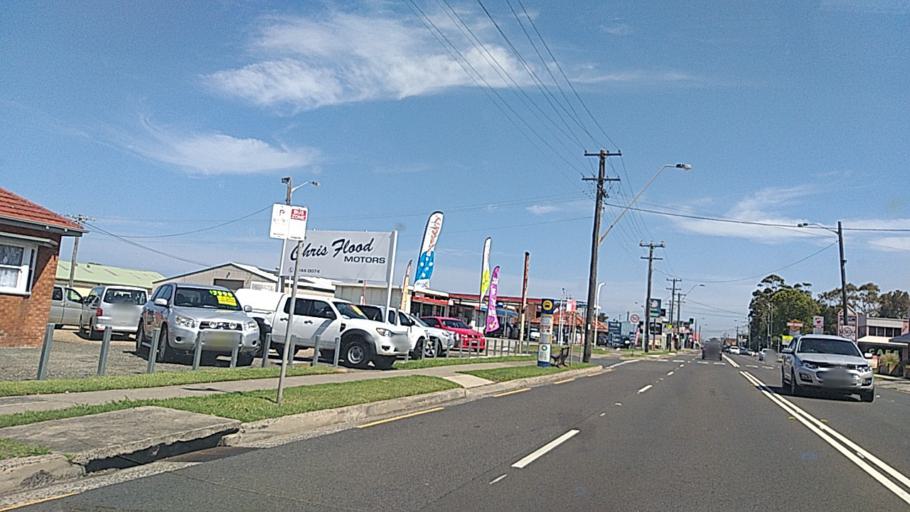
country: AU
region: New South Wales
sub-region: Wollongong
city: Fairy Meadow
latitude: -34.3885
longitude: 150.8940
